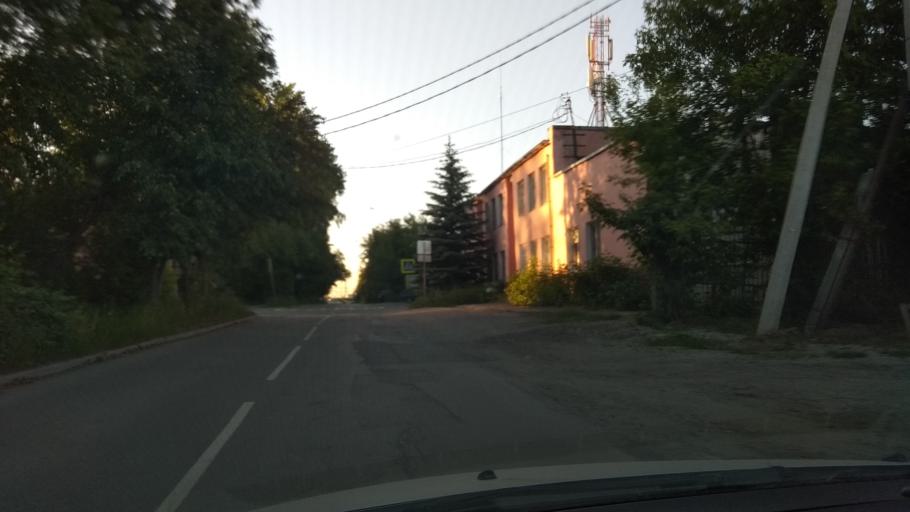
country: RU
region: Sverdlovsk
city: Sredneuralsk
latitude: 56.9865
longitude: 60.4599
